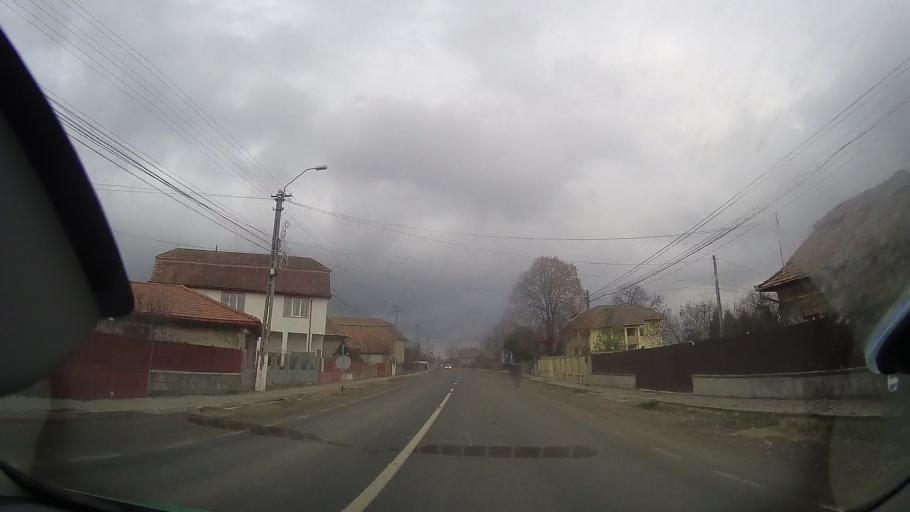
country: RO
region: Cluj
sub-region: Comuna Mihai Viteazu
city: Mihai Viteazu
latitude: 46.5407
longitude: 23.7569
